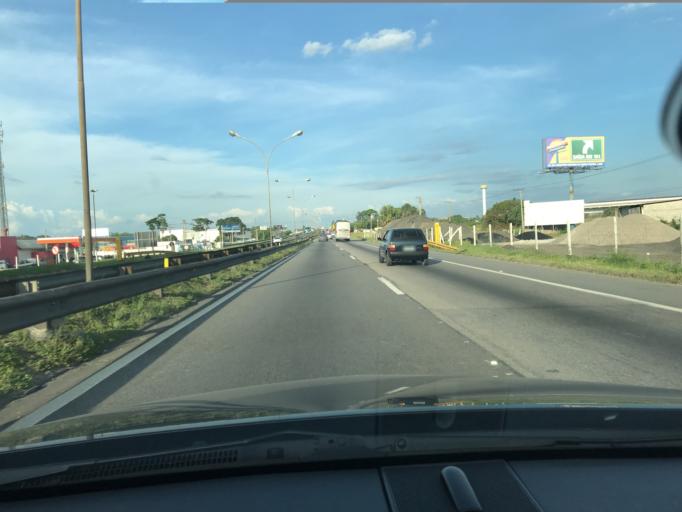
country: BR
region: Sao Paulo
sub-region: Jacarei
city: Jacarei
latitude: -23.2641
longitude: -45.9572
